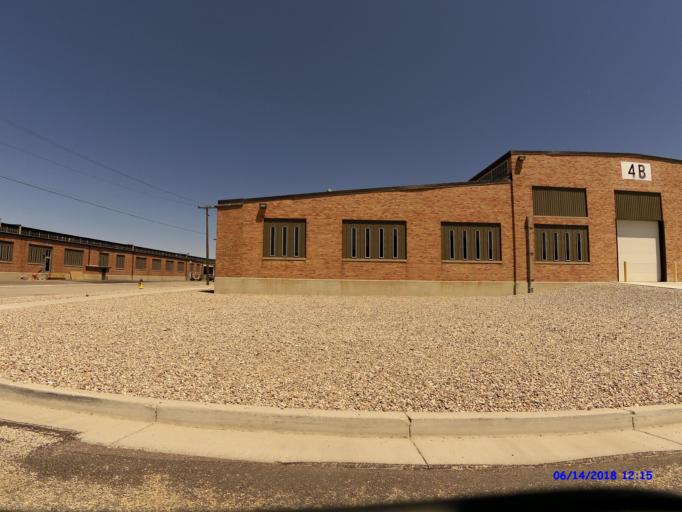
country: US
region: Utah
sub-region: Weber County
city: Harrisville
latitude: 41.2615
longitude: -111.9942
